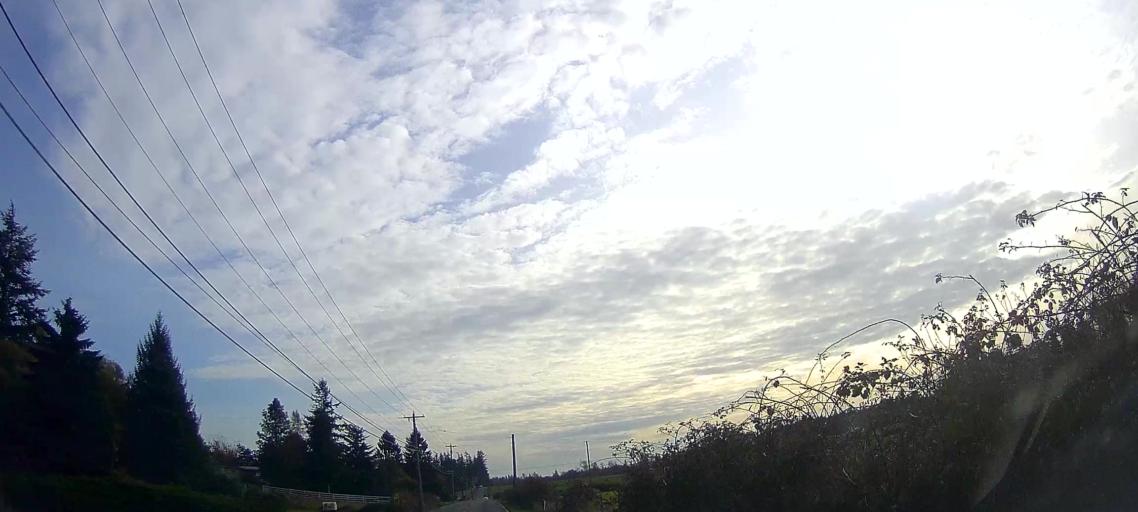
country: US
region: Washington
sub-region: Snohomish County
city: Stanwood
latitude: 48.2744
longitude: -122.3364
